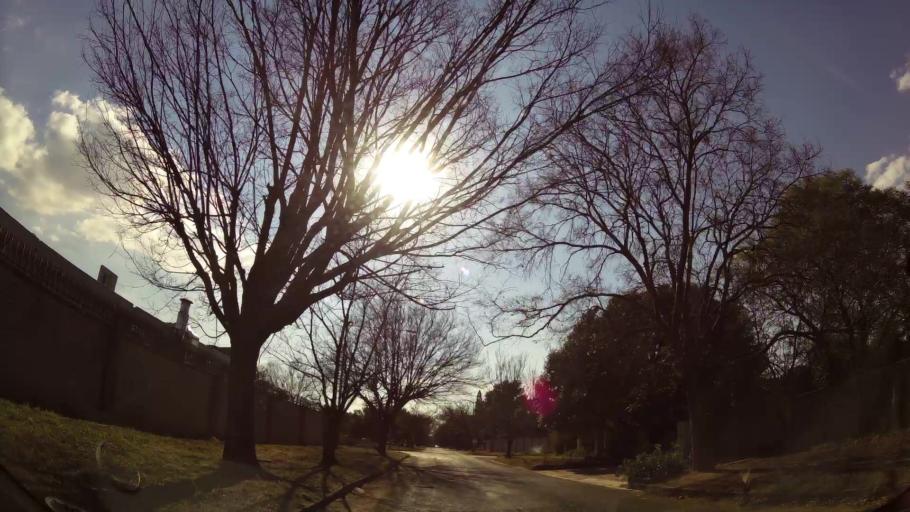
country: ZA
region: Gauteng
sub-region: Ekurhuleni Metropolitan Municipality
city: Benoni
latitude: -26.1478
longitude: 28.3428
